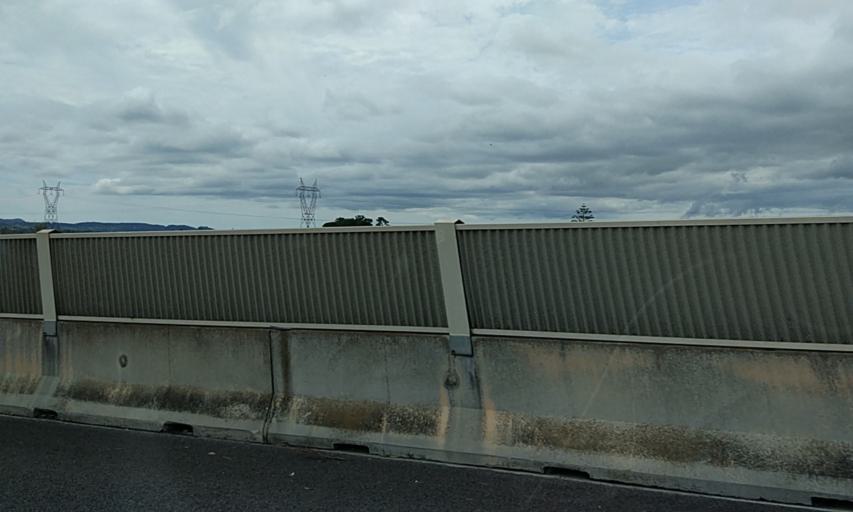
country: PT
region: Setubal
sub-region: Palmela
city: Pinhal Novo
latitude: 38.6289
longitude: -8.8665
